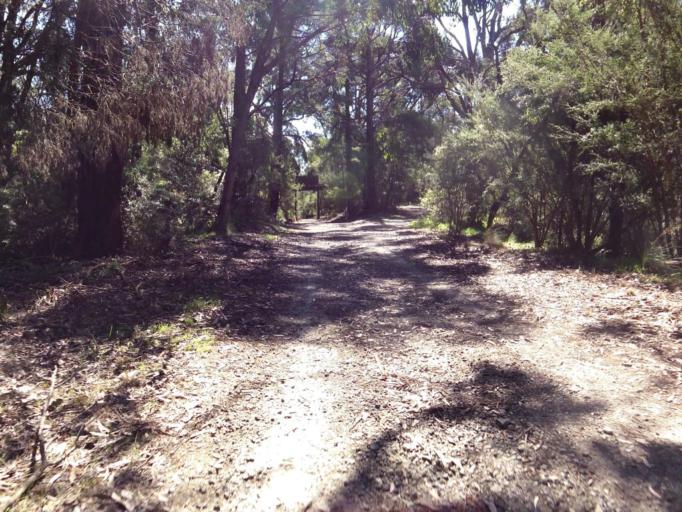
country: AU
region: Victoria
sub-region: Latrobe
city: Moe
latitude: -38.1743
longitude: 146.3328
